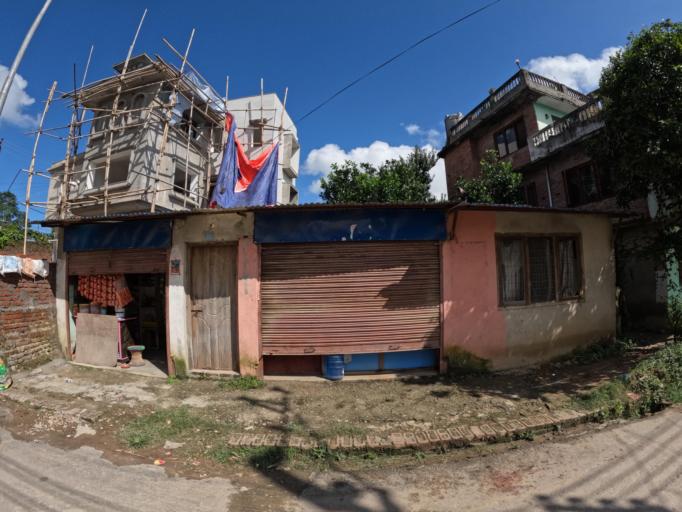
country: NP
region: Central Region
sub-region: Bagmati Zone
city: Kathmandu
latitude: 27.7509
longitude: 85.3345
